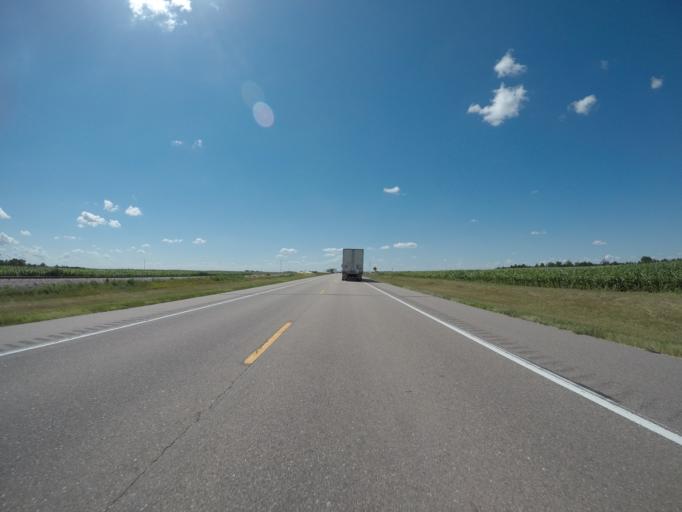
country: US
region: Nebraska
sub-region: Chase County
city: Imperial
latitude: 40.4986
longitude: -101.6071
